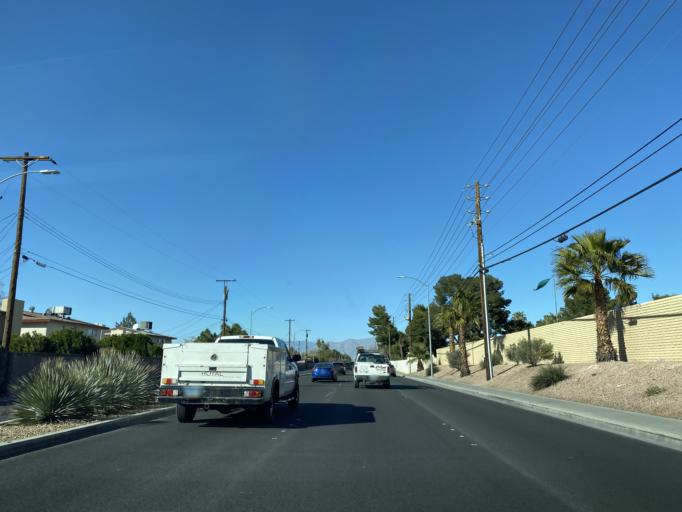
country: US
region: Nevada
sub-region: Clark County
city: Las Vegas
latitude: 36.1470
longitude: -115.1907
